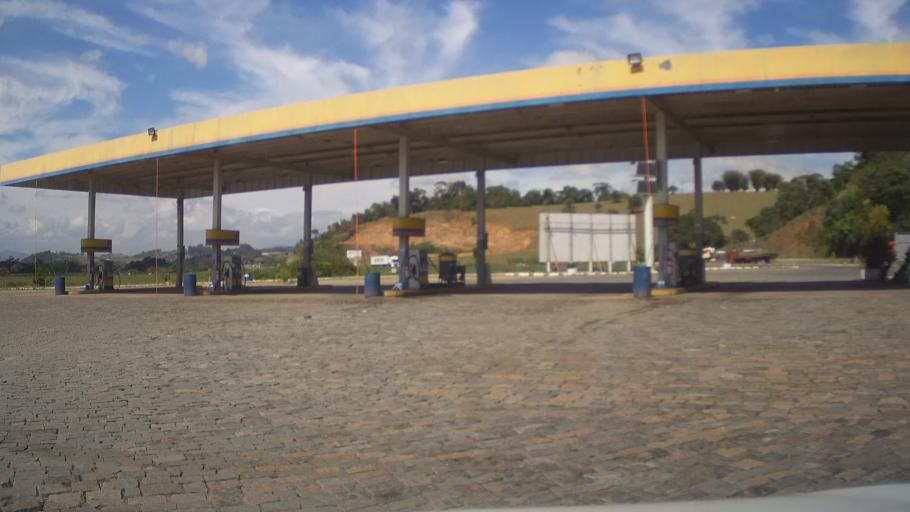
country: BR
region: Minas Gerais
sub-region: Cambui
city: Cambui
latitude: -22.5283
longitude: -46.0254
